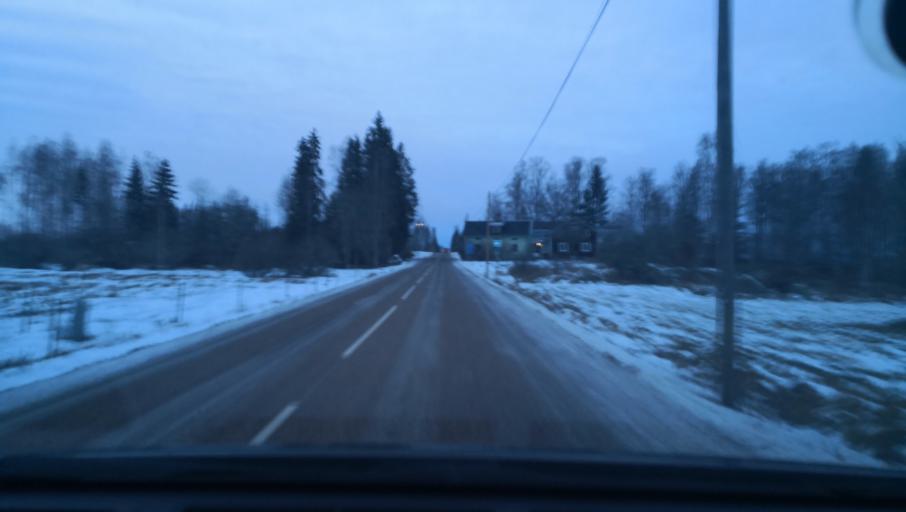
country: SE
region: Dalarna
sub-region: Avesta Kommun
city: Horndal
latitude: 60.1903
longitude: 16.4692
